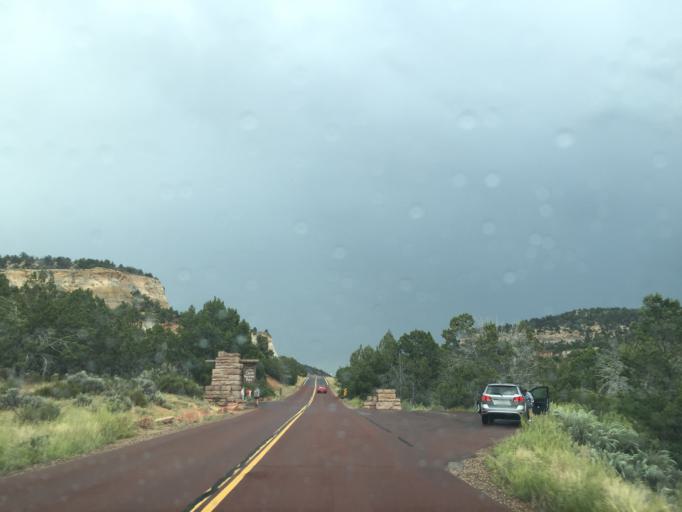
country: US
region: Utah
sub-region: Washington County
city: Hildale
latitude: 37.2353
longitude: -112.8651
